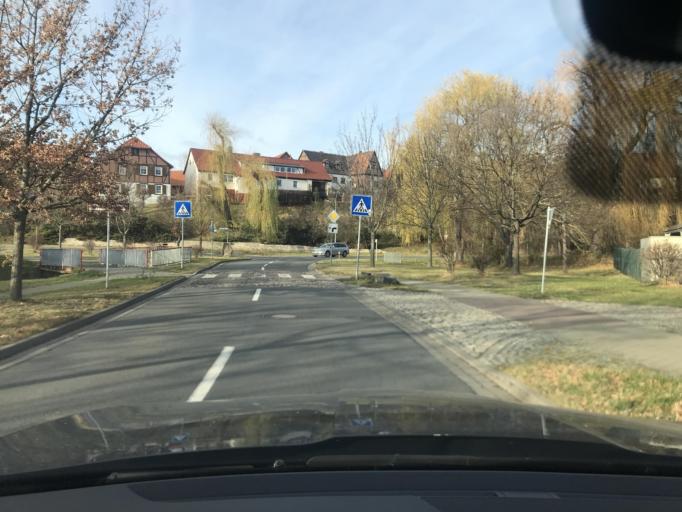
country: DE
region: Saxony-Anhalt
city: Weddersleben
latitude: 51.7637
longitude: 11.0877
